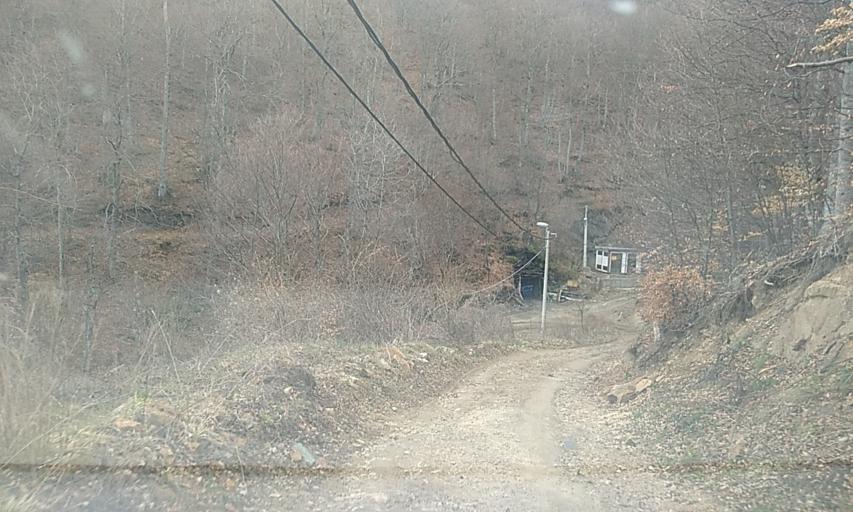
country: RS
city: Radovnica
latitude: 42.3494
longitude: 22.3395
